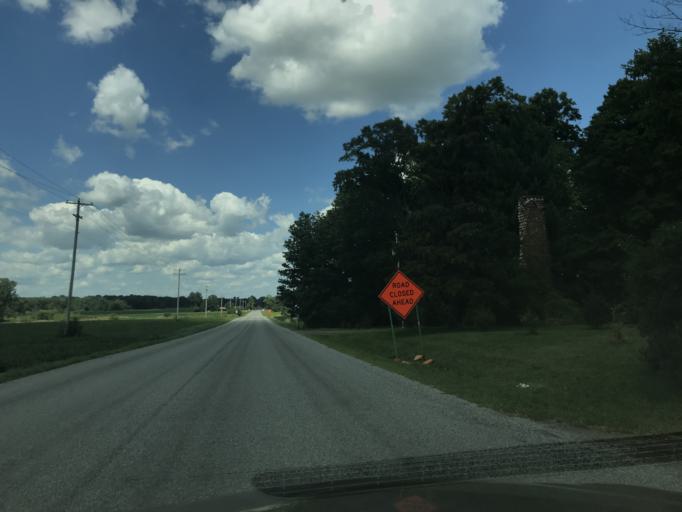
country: US
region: Michigan
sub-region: Ingham County
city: Holt
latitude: 42.5912
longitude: -84.5625
